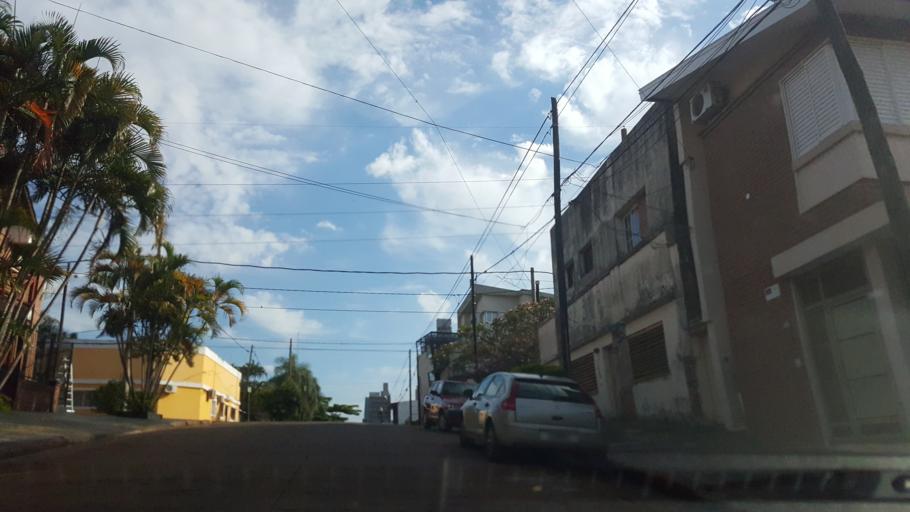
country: AR
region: Misiones
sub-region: Departamento de Capital
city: Posadas
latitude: -27.3588
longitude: -55.8925
